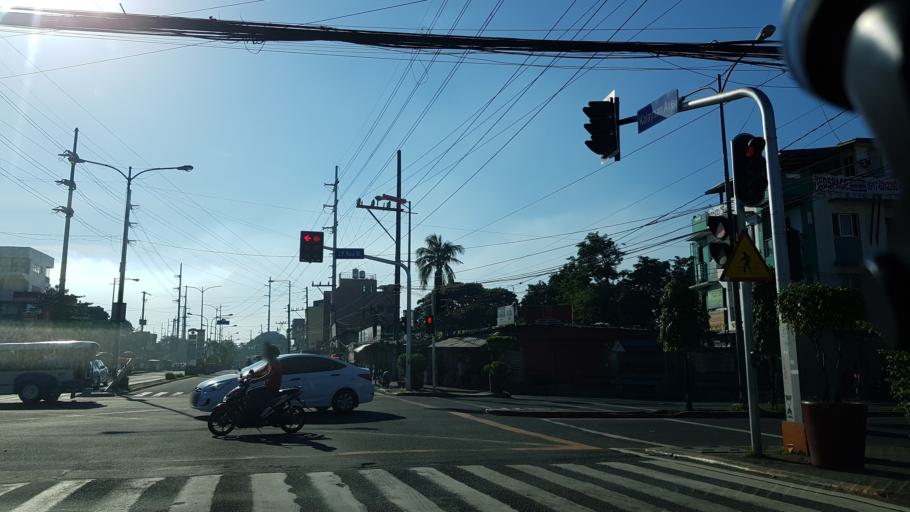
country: PH
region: Calabarzon
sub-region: Province of Rizal
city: Pateros
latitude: 14.5552
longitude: 121.0644
